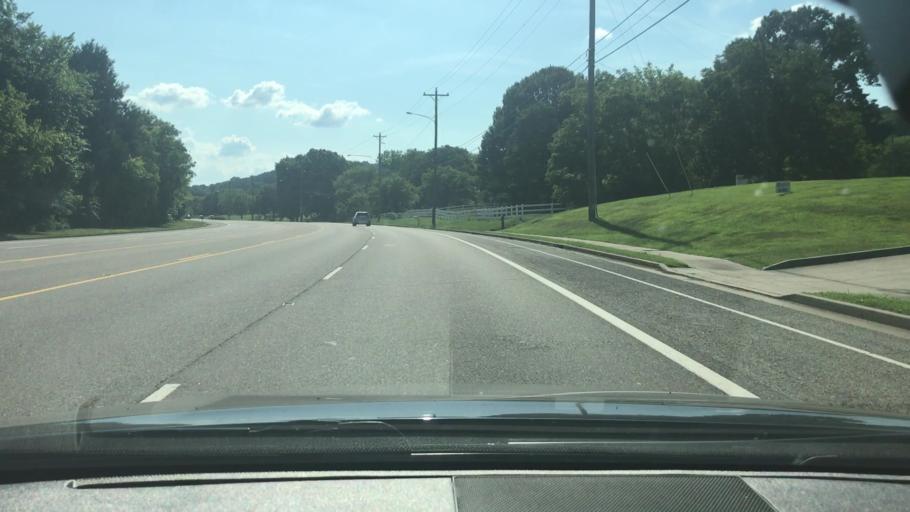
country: US
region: Tennessee
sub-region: Davidson County
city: Belle Meade
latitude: 36.2115
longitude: -86.9240
